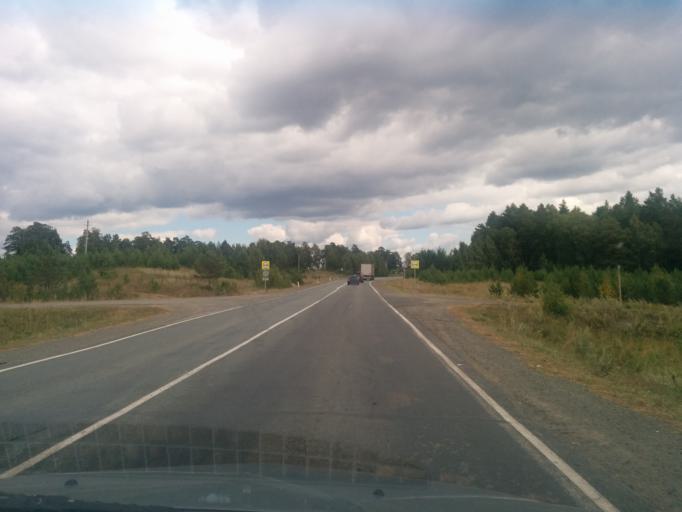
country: RU
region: Bashkortostan
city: Lomovka
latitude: 53.8966
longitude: 58.0869
